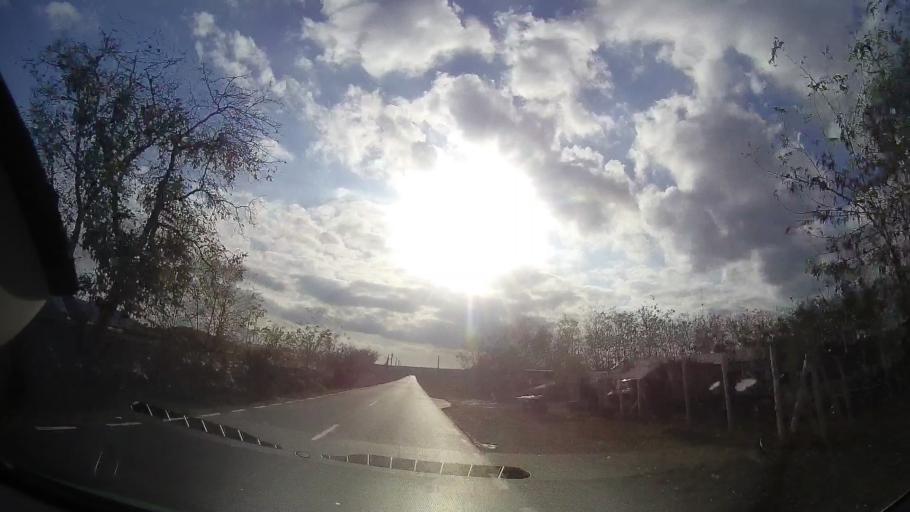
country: RO
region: Constanta
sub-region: Comuna Albesti
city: Albesti
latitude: 43.8101
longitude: 28.4362
